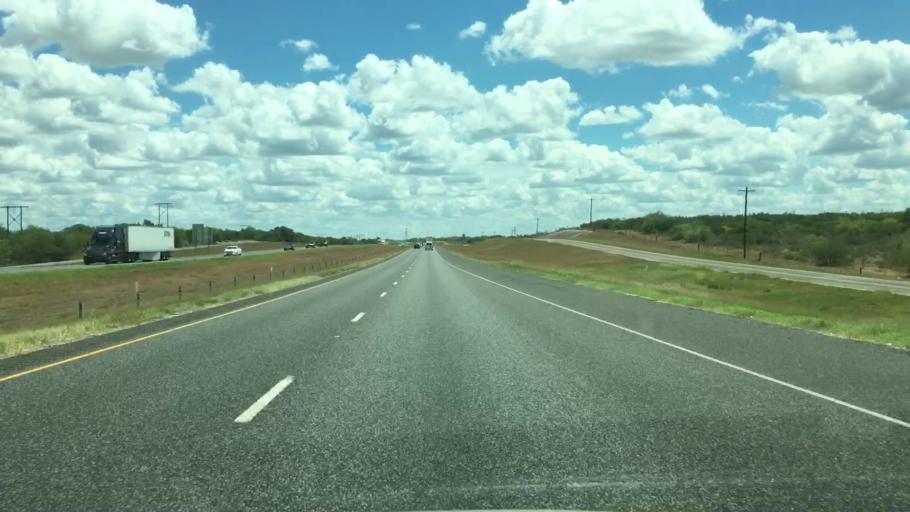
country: US
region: Texas
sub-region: Atascosa County
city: Pleasanton
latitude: 28.8400
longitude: -98.3750
